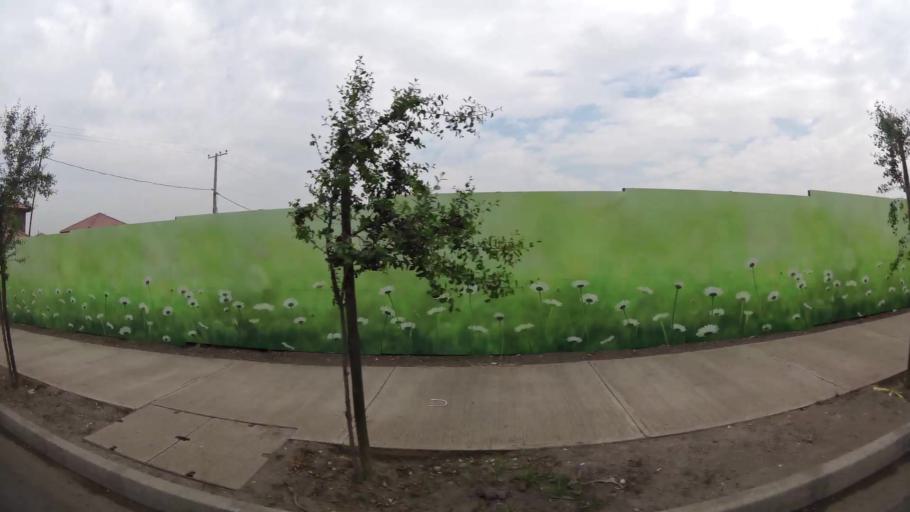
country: CL
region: Santiago Metropolitan
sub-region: Provincia de Chacabuco
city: Chicureo Abajo
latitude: -33.2189
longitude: -70.6735
